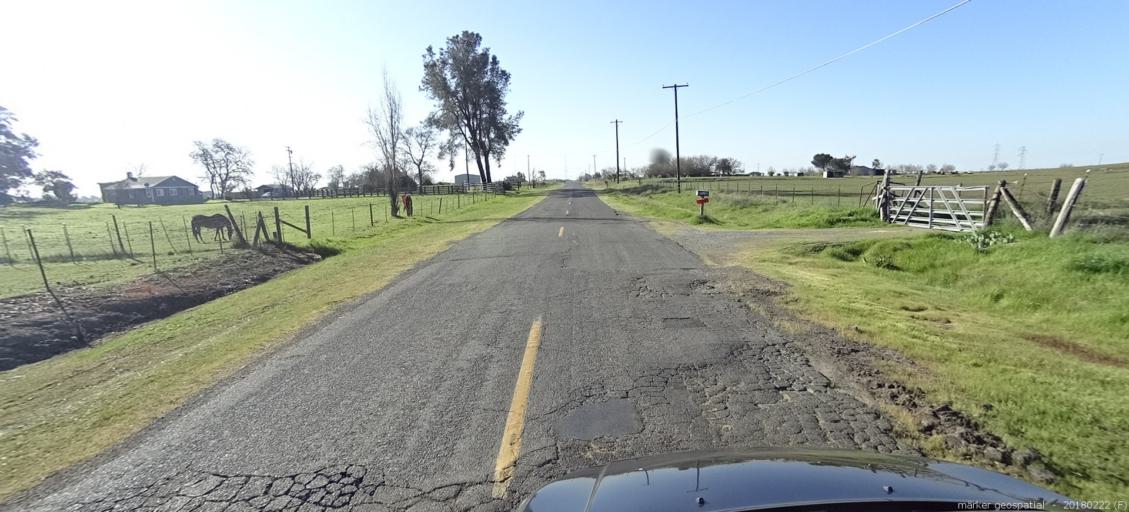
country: US
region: California
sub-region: Sacramento County
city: Elverta
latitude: 38.7291
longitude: -121.4844
